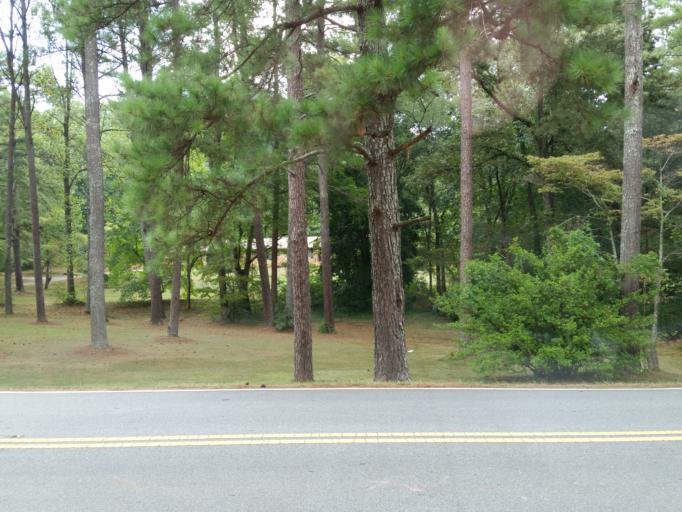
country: US
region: Georgia
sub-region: Cherokee County
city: Woodstock
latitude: 34.0457
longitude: -84.5103
